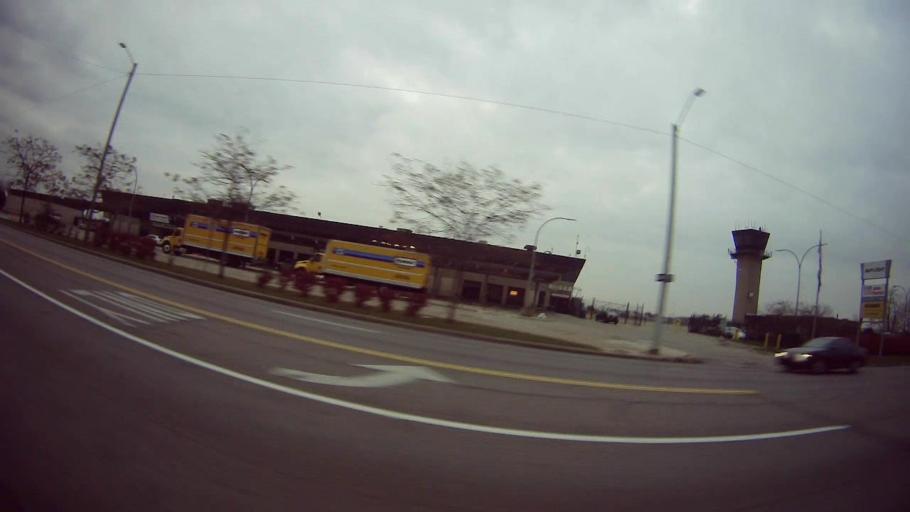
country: US
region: Michigan
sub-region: Wayne County
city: Hamtramck
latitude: 42.4097
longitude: -83.0035
